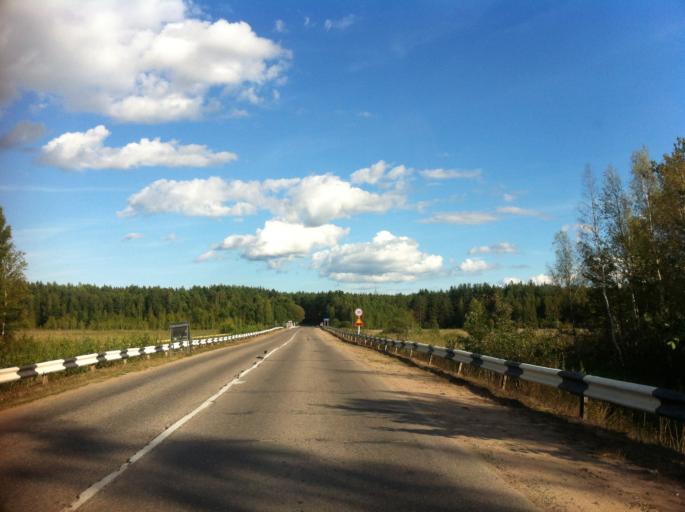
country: RU
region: Pskov
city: Izborsk
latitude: 57.8364
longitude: 27.9296
